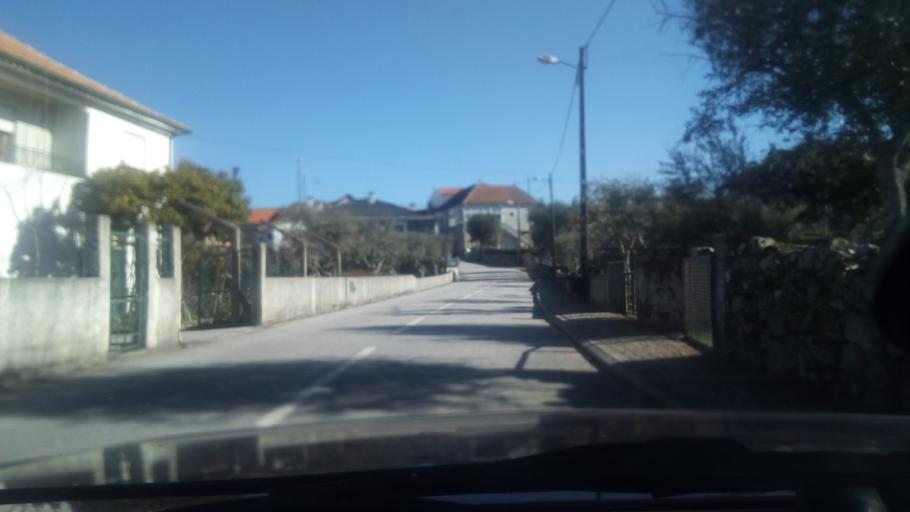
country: PT
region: Guarda
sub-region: Fornos de Algodres
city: Fornos de Algodres
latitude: 40.6076
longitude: -7.5100
